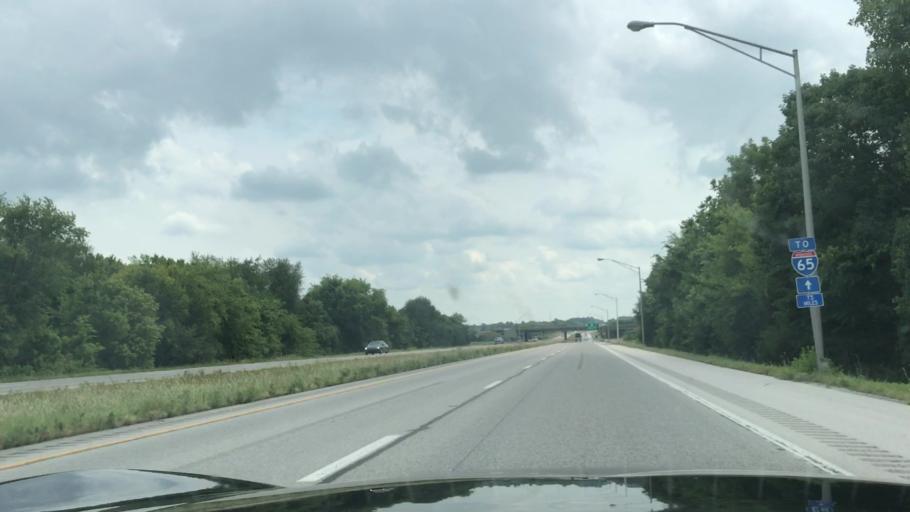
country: US
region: Kentucky
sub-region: Warren County
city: Bowling Green
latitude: 36.9966
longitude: -86.5053
